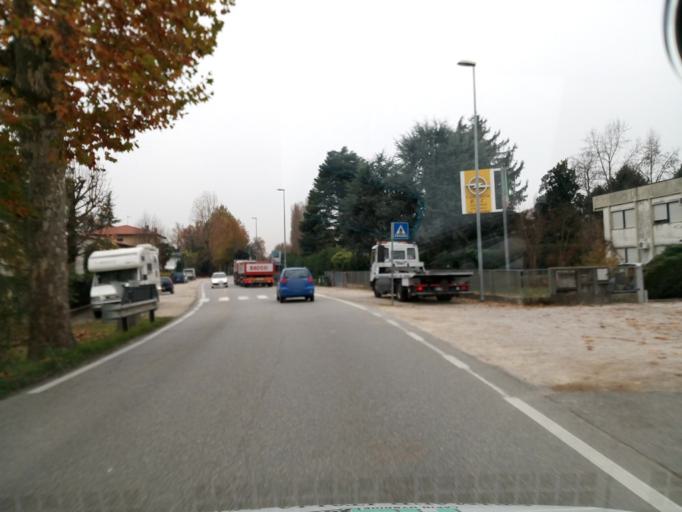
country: IT
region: Veneto
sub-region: Provincia di Padova
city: Vigonza
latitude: 45.4404
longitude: 11.9622
